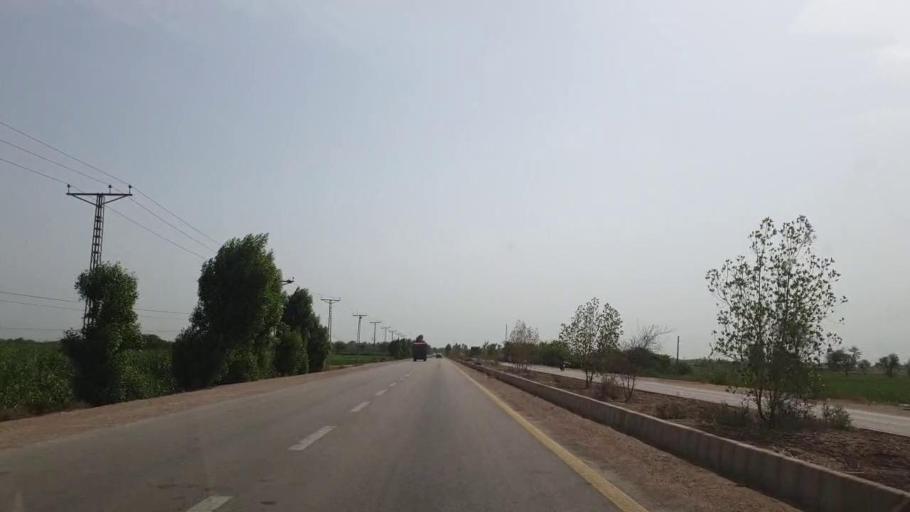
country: PK
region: Sindh
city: Sakrand
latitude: 26.2046
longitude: 68.3173
